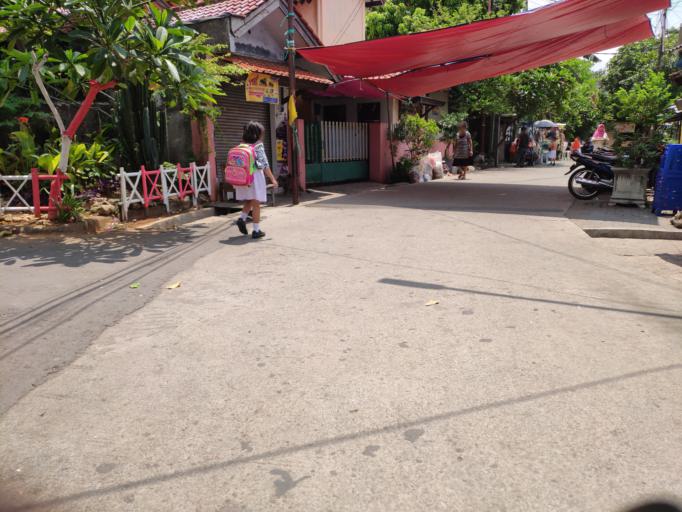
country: ID
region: Jakarta Raya
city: Jakarta
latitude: -6.2140
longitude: 106.8711
